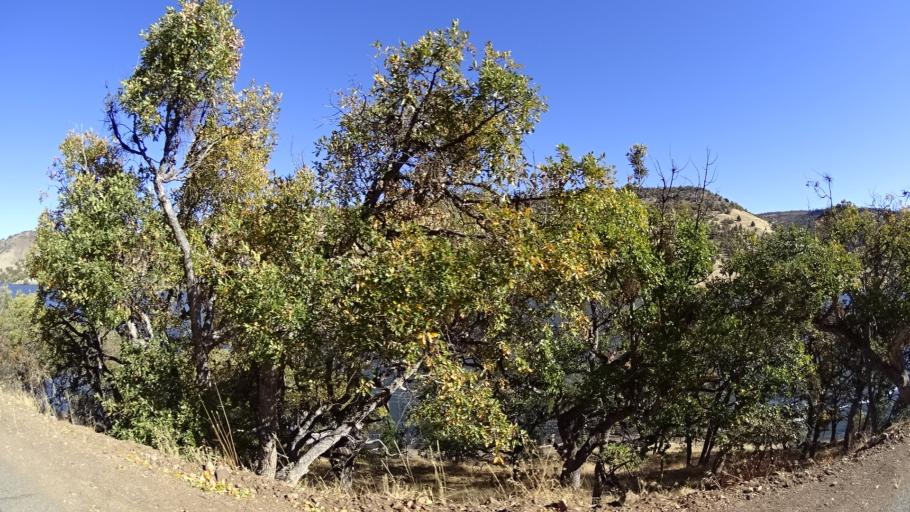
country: US
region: California
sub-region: Siskiyou County
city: Montague
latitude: 41.9735
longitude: -122.2901
